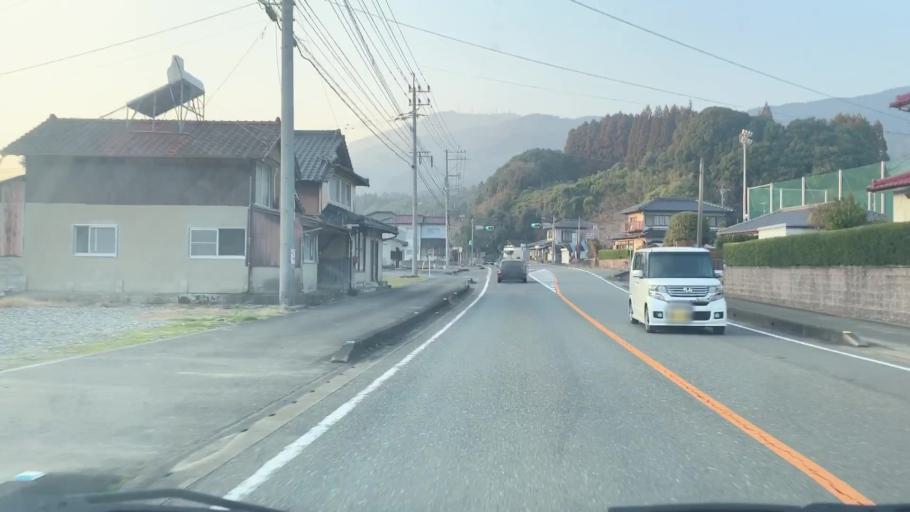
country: JP
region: Saga Prefecture
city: Takeocho-takeo
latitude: 33.2622
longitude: 130.0581
